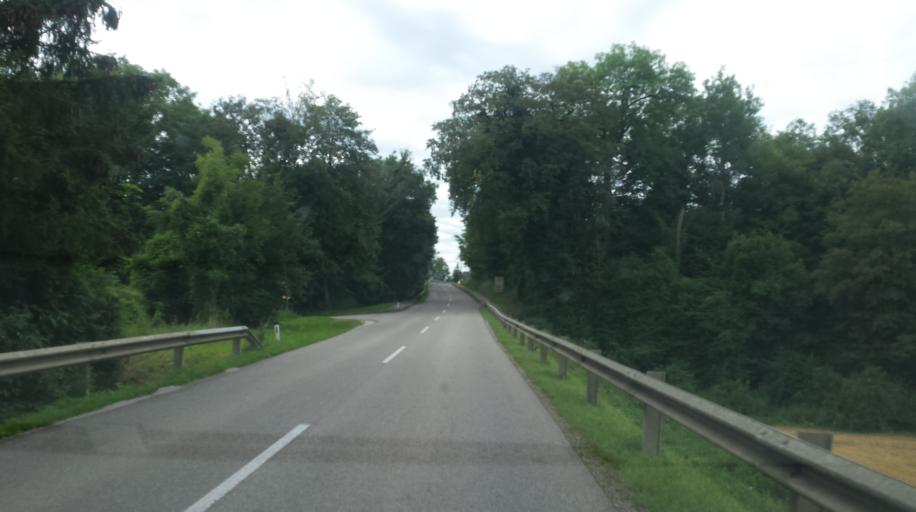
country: AT
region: Upper Austria
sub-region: Wels-Land
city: Bad Wimsbach-Neydharting
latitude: 48.0659
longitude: 13.9087
